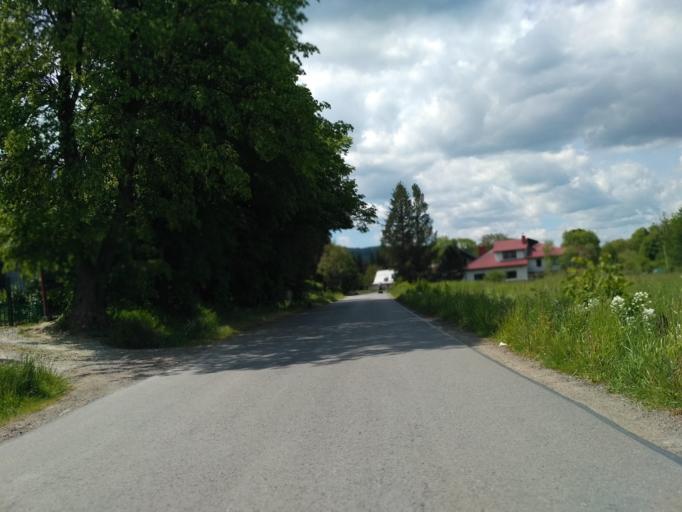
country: PL
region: Subcarpathian Voivodeship
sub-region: Powiat krosnienski
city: Dukla
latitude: 49.5548
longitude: 21.6708
